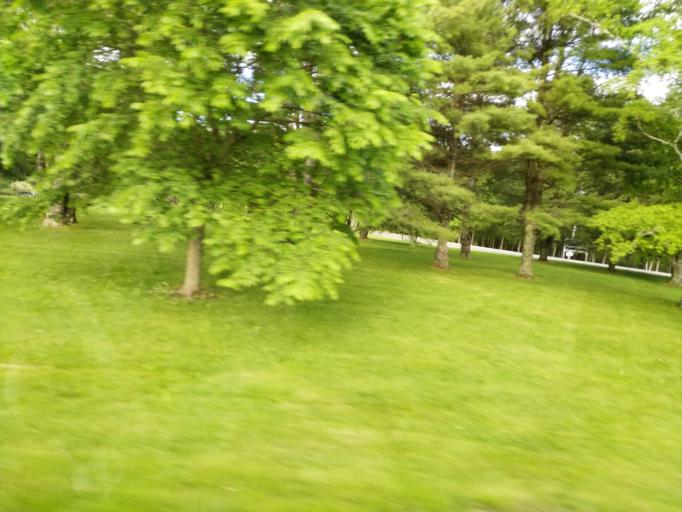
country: US
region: Maine
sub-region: Cumberland County
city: New Gloucester
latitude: 43.9018
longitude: -70.2545
